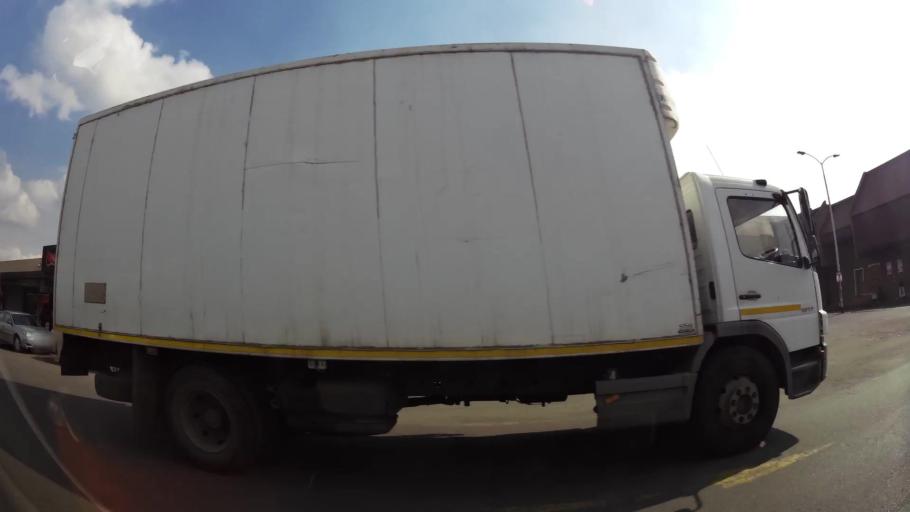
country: ZA
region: Gauteng
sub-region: Sedibeng District Municipality
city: Vereeniging
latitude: -26.6770
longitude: 27.9333
